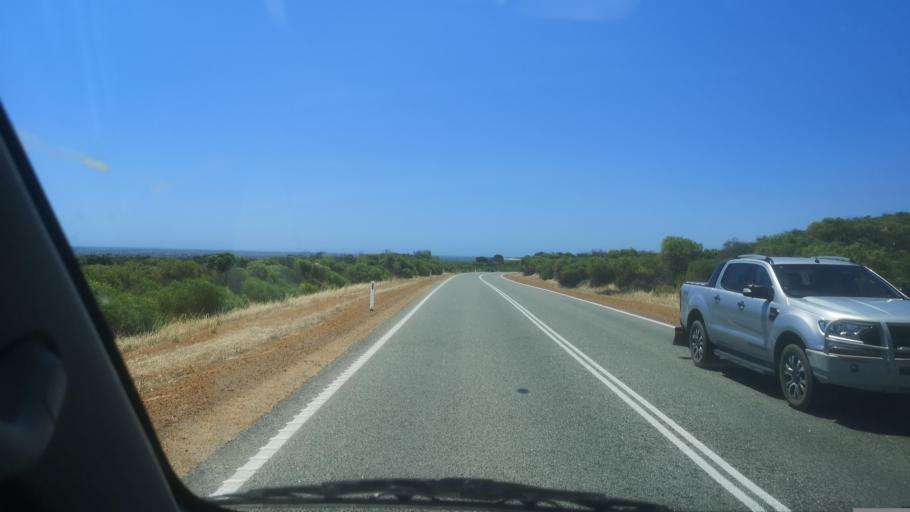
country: AU
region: Western Australia
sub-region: Dandaragan
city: Jurien Bay
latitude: -30.0164
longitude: 114.9714
